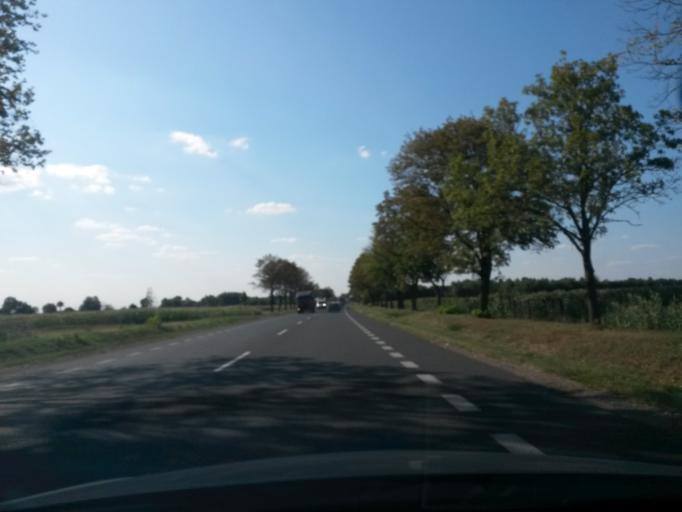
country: PL
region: Masovian Voivodeship
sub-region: Powiat sierpecki
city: Zawidz
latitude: 52.7954
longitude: 19.8678
